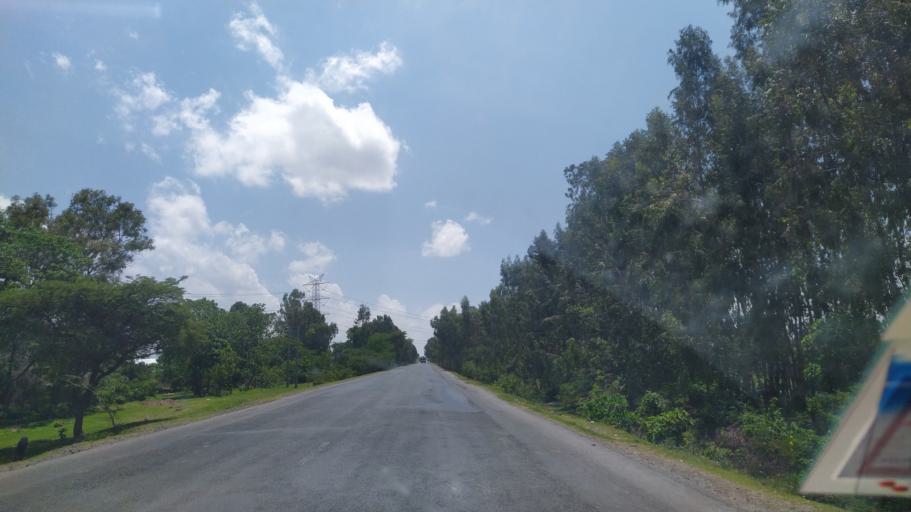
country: ET
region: Southern Nations, Nationalities, and People's Region
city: Butajira
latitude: 7.7516
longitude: 38.1284
